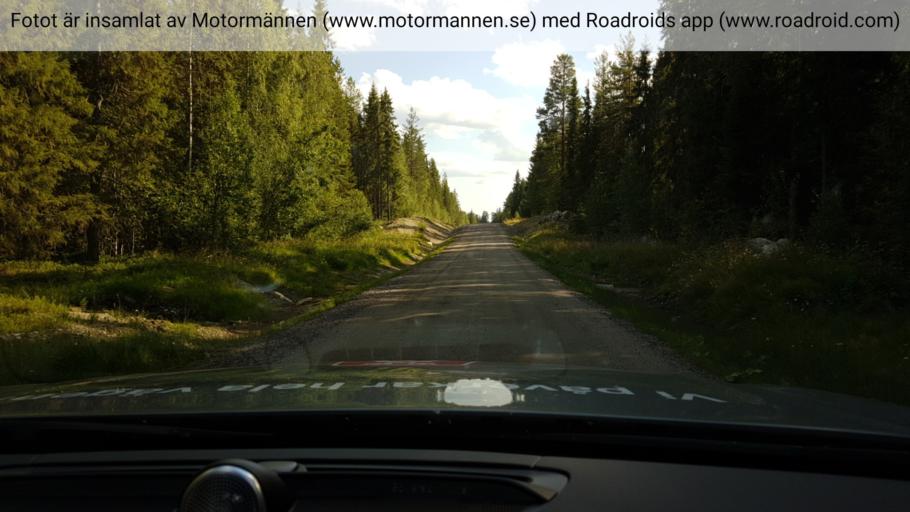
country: SE
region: Vaesterbotten
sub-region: Dorotea Kommun
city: Dorotea
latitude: 63.9514
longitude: 16.0784
